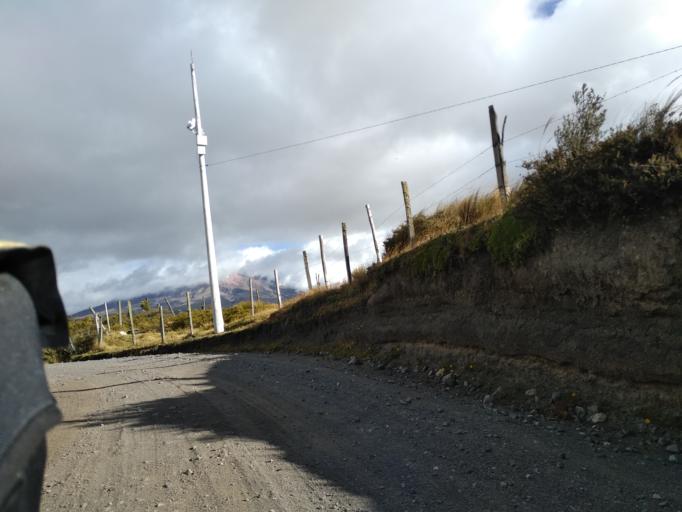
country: EC
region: Pichincha
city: Machachi
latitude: -0.5613
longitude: -78.4478
